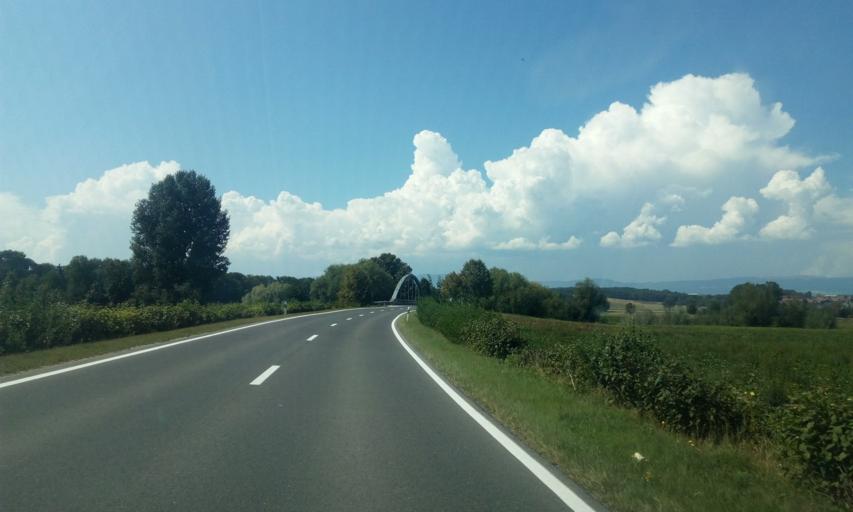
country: CH
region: Fribourg
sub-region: Broye District
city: Domdidier
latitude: 46.8891
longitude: 7.0114
